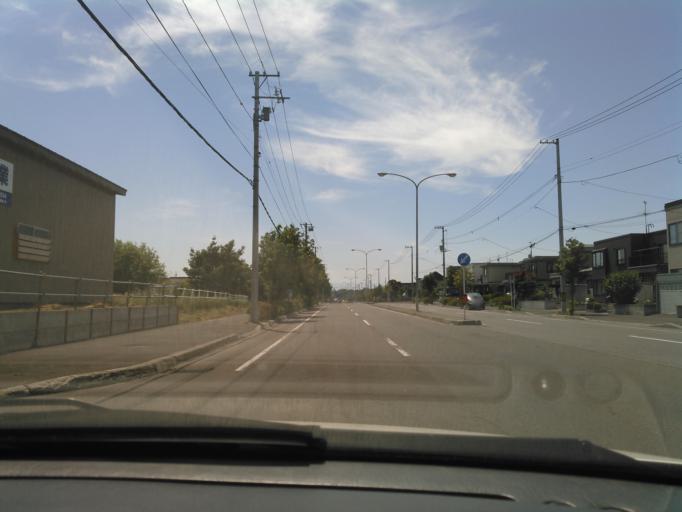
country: JP
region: Hokkaido
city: Ebetsu
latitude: 43.1023
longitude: 141.5613
